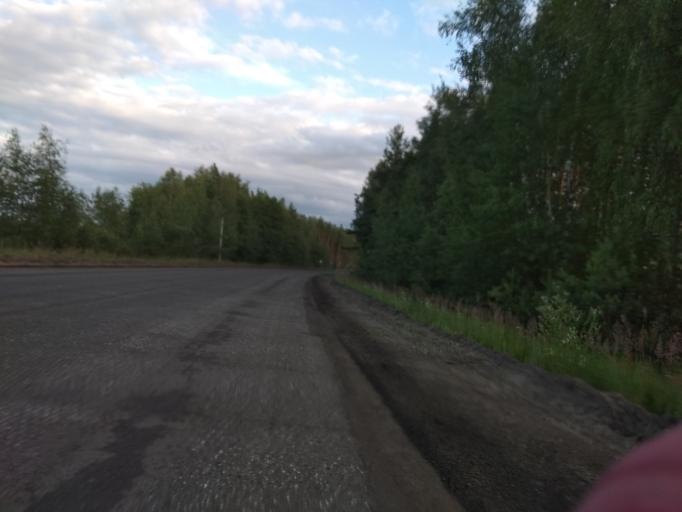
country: RU
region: Moskovskaya
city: Misheronskiy
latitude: 55.6478
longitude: 39.7572
